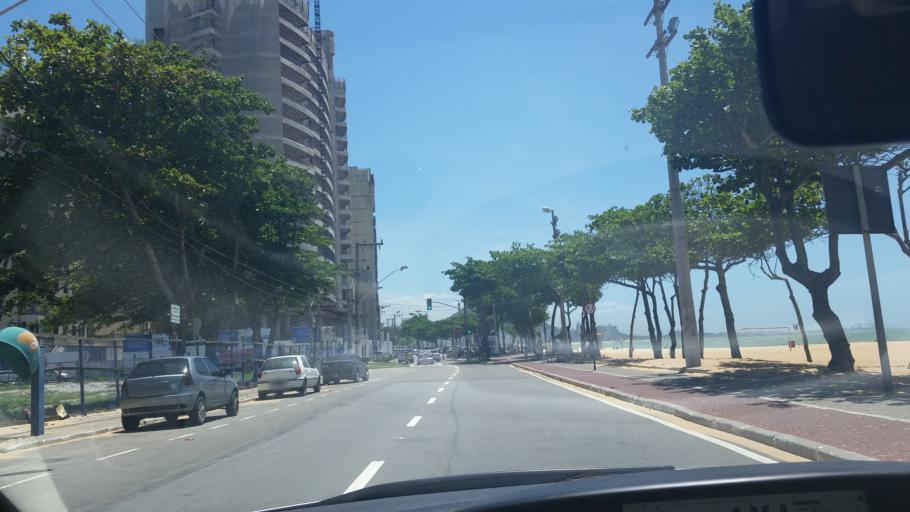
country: BR
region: Espirito Santo
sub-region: Vila Velha
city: Vila Velha
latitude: -20.3532
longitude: -40.2841
